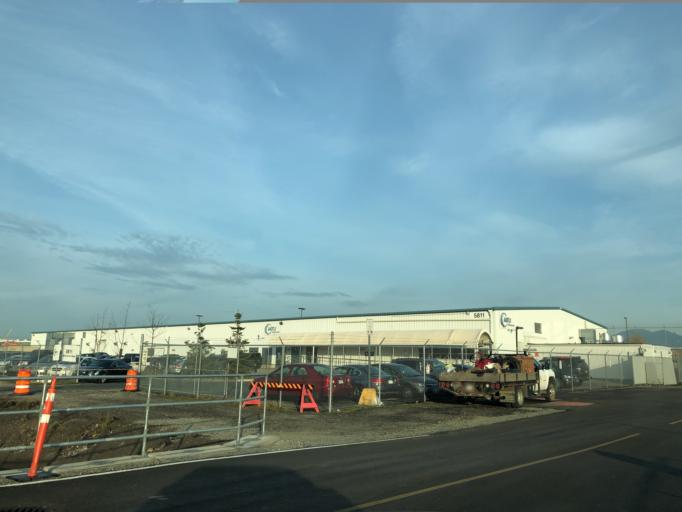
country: CA
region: British Columbia
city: Richmond
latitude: 49.1939
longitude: -123.1674
